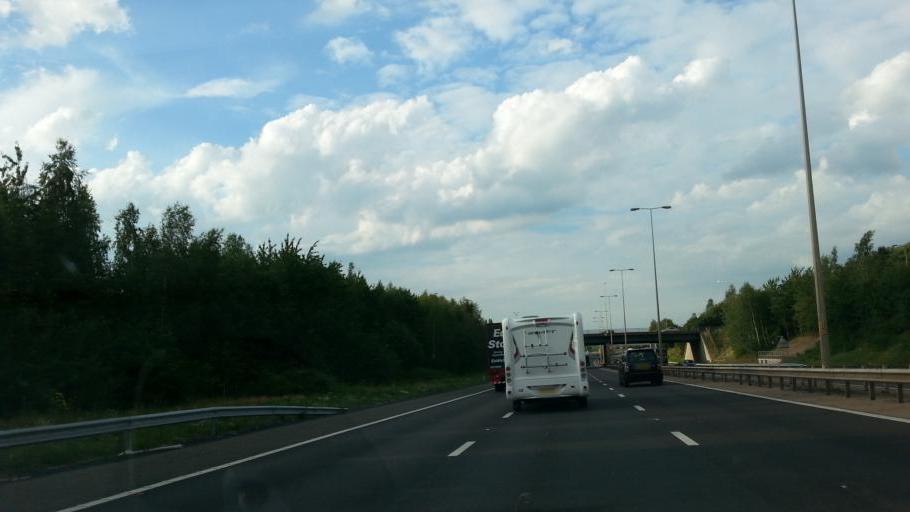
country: GB
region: England
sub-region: Worcestershire
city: Fernhill Heath
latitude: 52.2104
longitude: -2.1592
